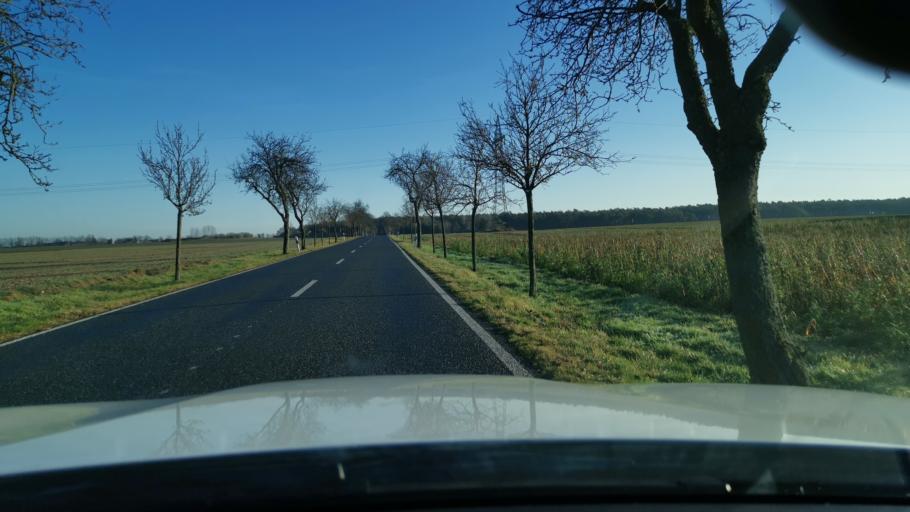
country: DE
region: Saxony-Anhalt
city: Zahna
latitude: 51.9731
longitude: 12.8124
